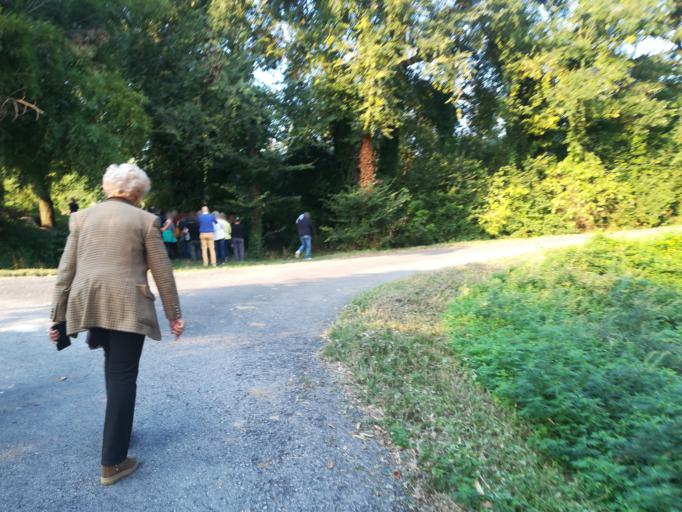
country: IT
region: The Marches
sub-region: Provincia di Macerata
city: Sforzacosta
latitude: 43.2630
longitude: 13.4308
